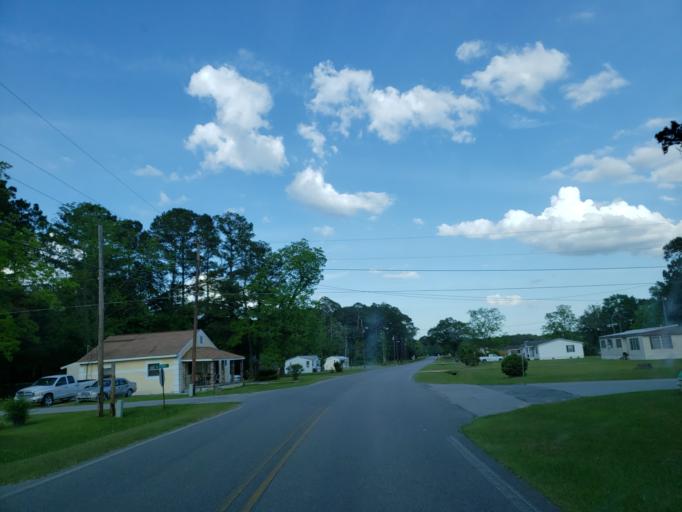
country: US
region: Georgia
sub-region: Lowndes County
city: Hahira
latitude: 31.0467
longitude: -83.3875
